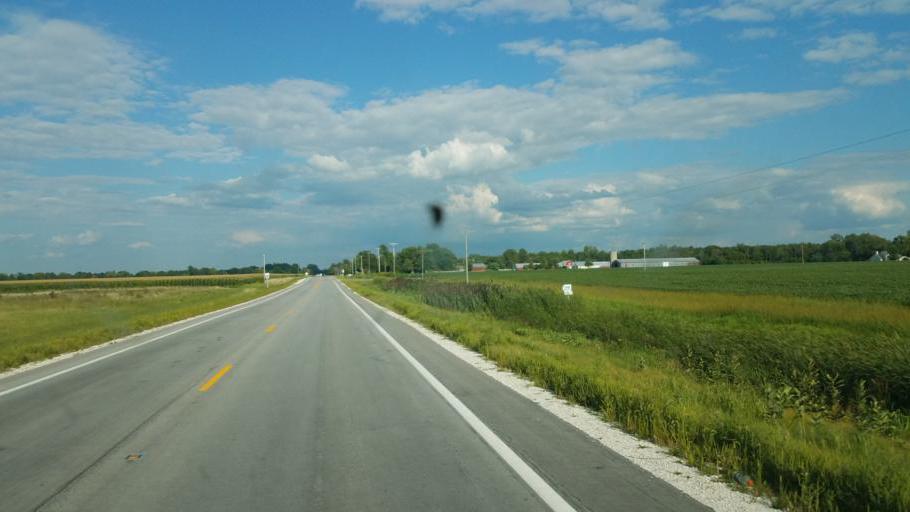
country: US
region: Ohio
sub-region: Sandusky County
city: Stony Prairie
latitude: 41.3418
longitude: -83.2066
